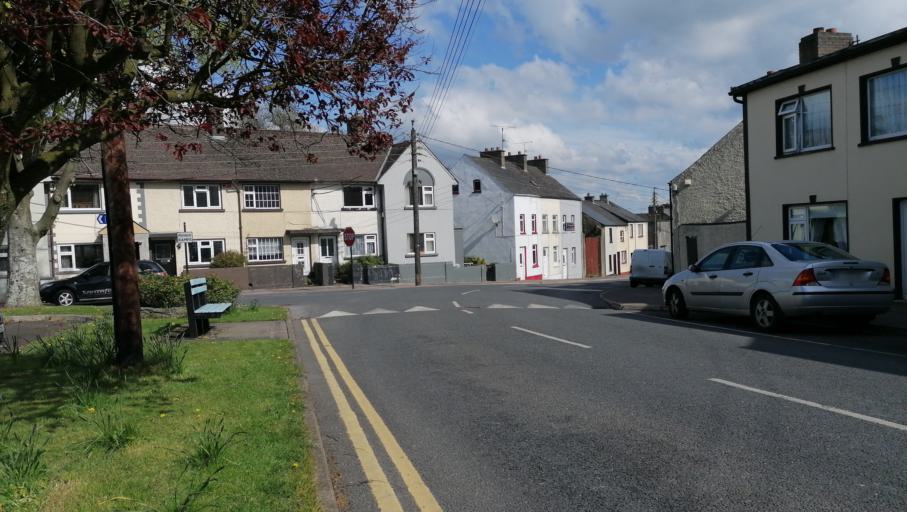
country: IE
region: Ulster
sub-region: County Monaghan
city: Castleblayney
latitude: 54.1189
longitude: -6.7342
